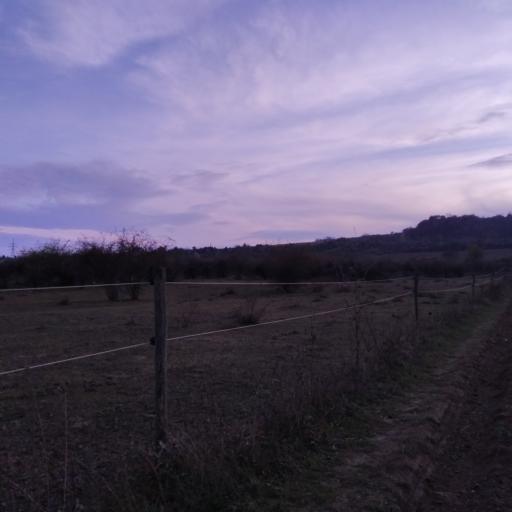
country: HU
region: Pest
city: Pomaz
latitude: 47.6237
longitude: 19.0250
